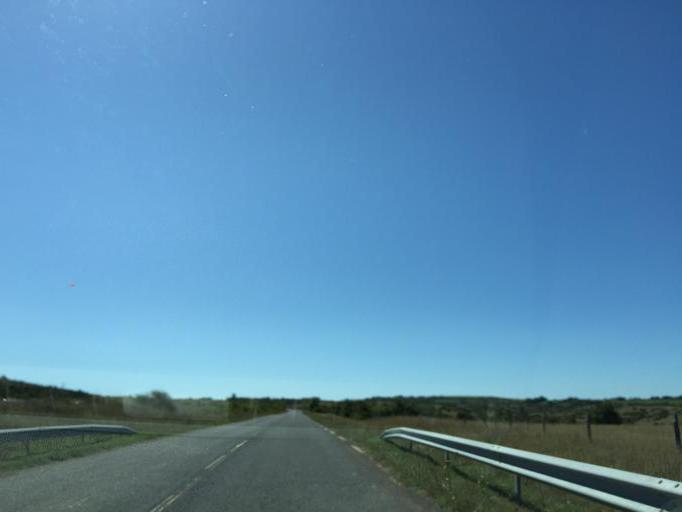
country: FR
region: Midi-Pyrenees
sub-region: Departement de l'Aveyron
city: La Cavalerie
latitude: 43.9154
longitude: 3.2526
